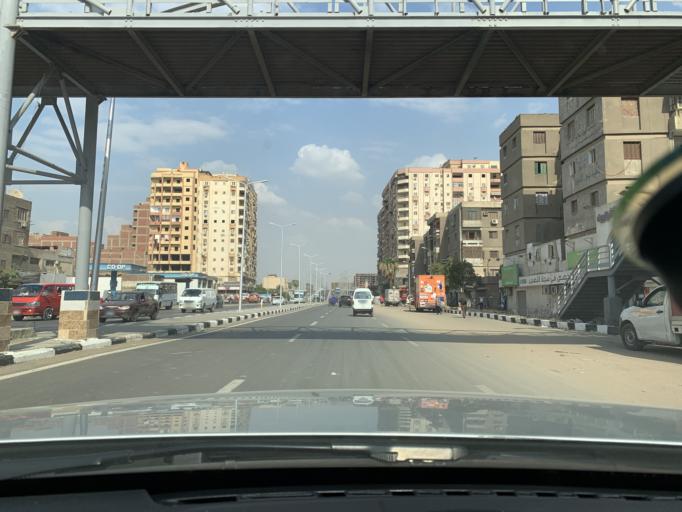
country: EG
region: Muhafazat al Qahirah
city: Cairo
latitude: 30.1318
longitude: 31.2844
